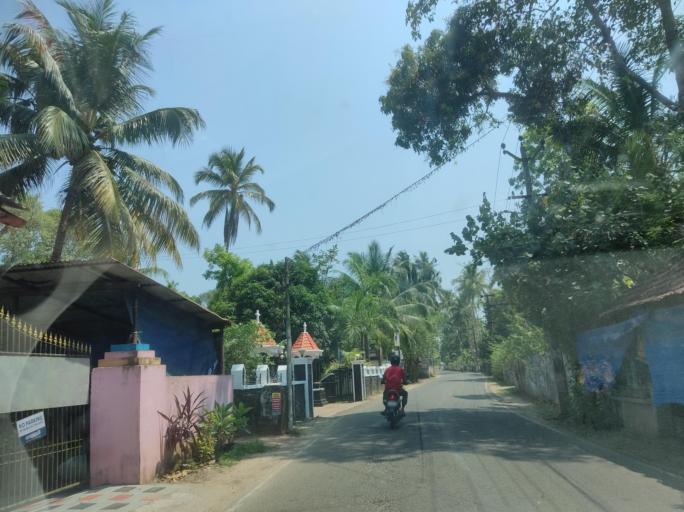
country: IN
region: Kerala
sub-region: Alappuzha
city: Kutiatodu
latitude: 9.7843
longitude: 76.3042
